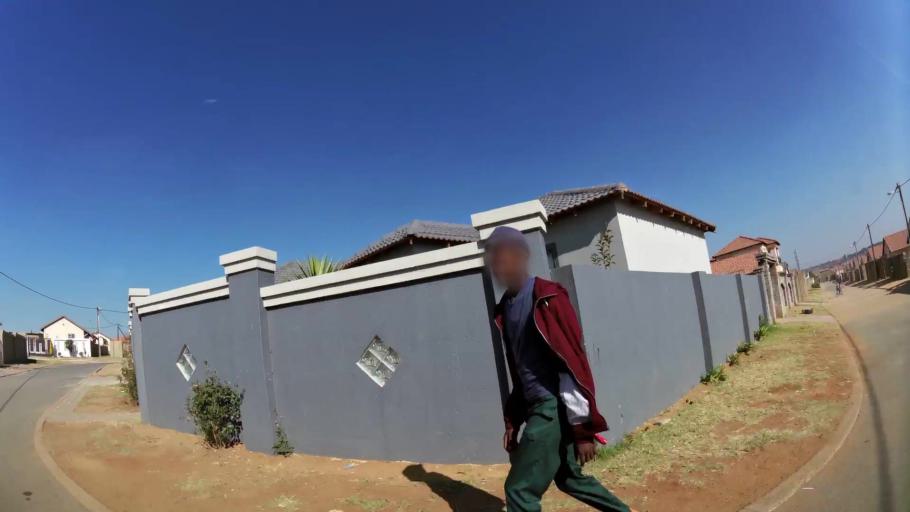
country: ZA
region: Gauteng
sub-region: West Rand District Municipality
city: Muldersdriseloop
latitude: -26.0349
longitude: 27.9256
